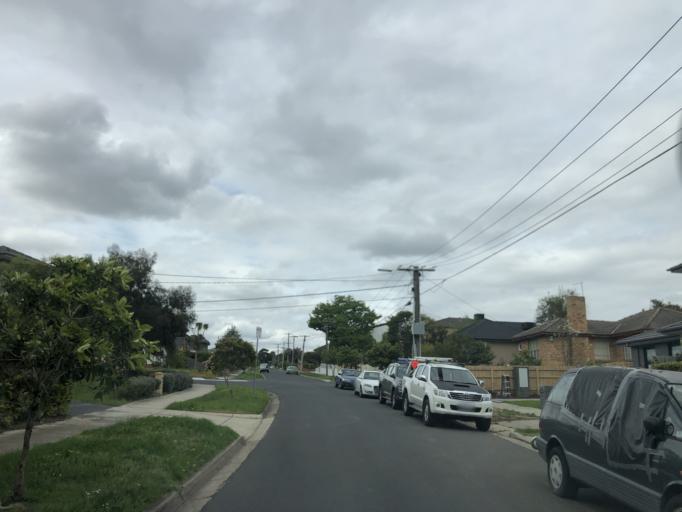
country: AU
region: Victoria
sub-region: Monash
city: Ashwood
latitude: -37.8694
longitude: 145.1014
